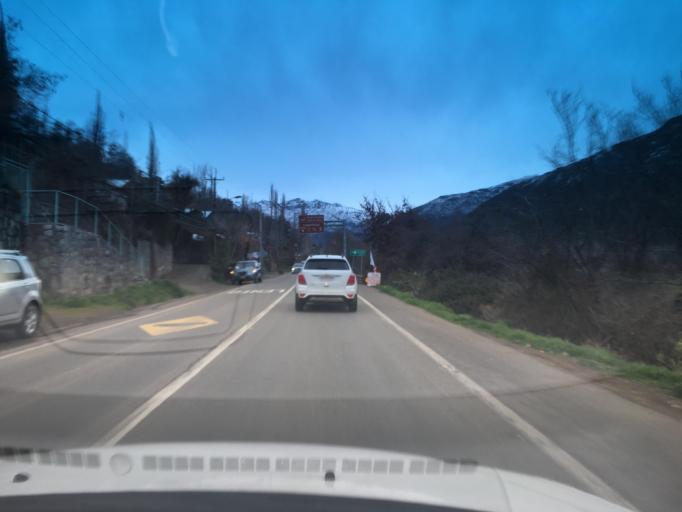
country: CL
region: Santiago Metropolitan
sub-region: Provincia de Cordillera
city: Puente Alto
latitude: -33.6476
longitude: -70.3511
